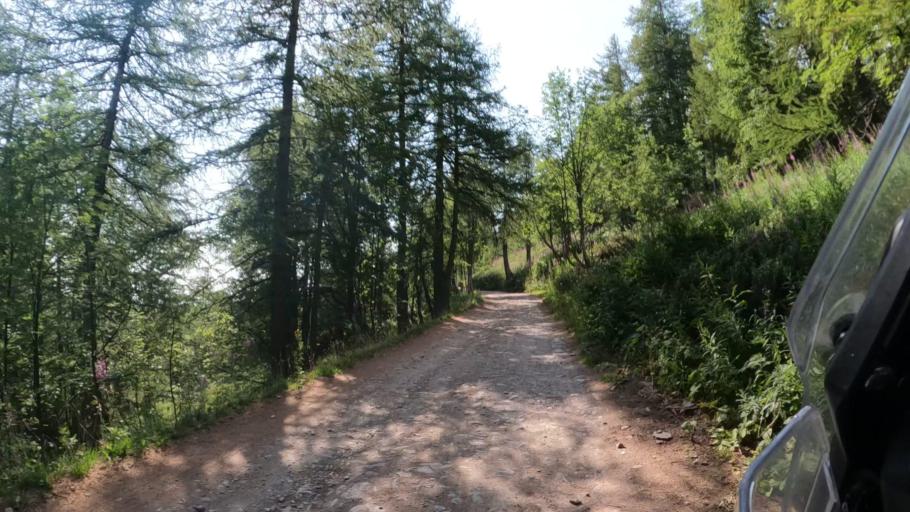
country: IT
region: Piedmont
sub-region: Provincia di Cuneo
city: Briga Alta
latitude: 44.1142
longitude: 7.7018
